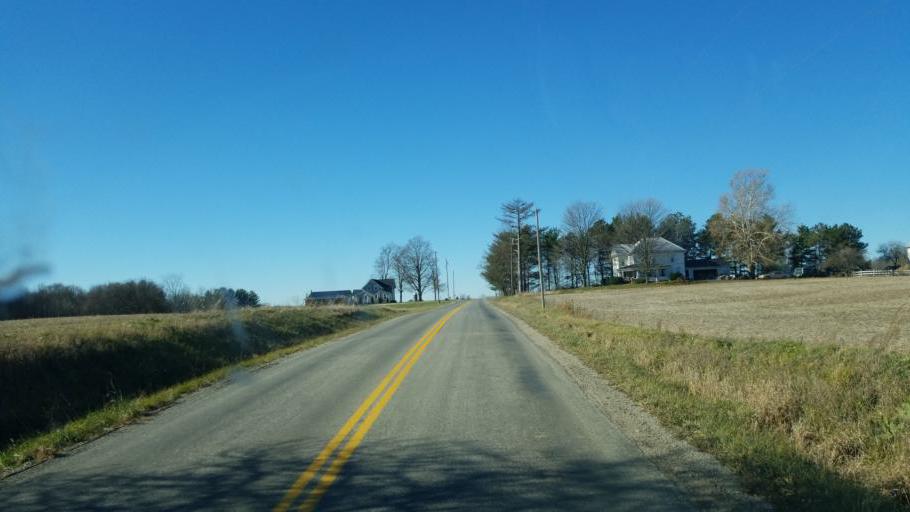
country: US
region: Ohio
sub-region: Ashland County
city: Ashland
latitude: 40.9532
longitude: -82.3842
